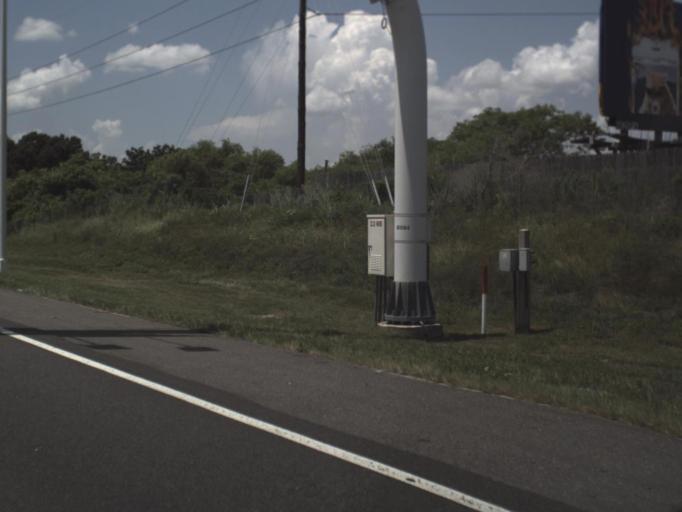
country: US
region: Florida
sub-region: Hillsborough County
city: East Lake-Orient Park
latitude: 27.9718
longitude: -82.3971
